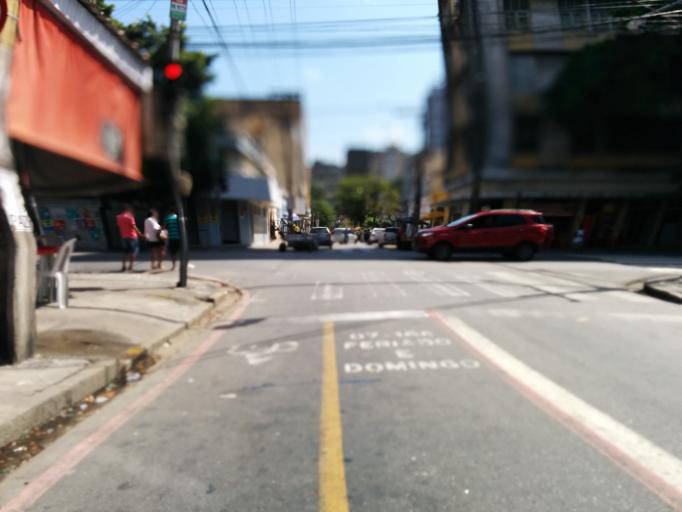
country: BR
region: Pernambuco
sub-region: Recife
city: Recife
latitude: -8.0586
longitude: -34.8811
